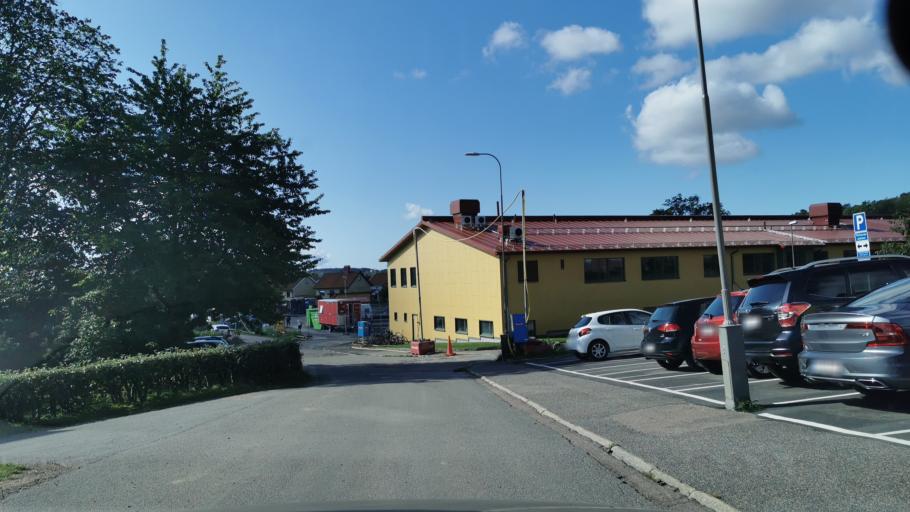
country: SE
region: Vaestra Goetaland
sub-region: Goteborg
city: Majorna
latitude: 57.6557
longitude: 11.9297
